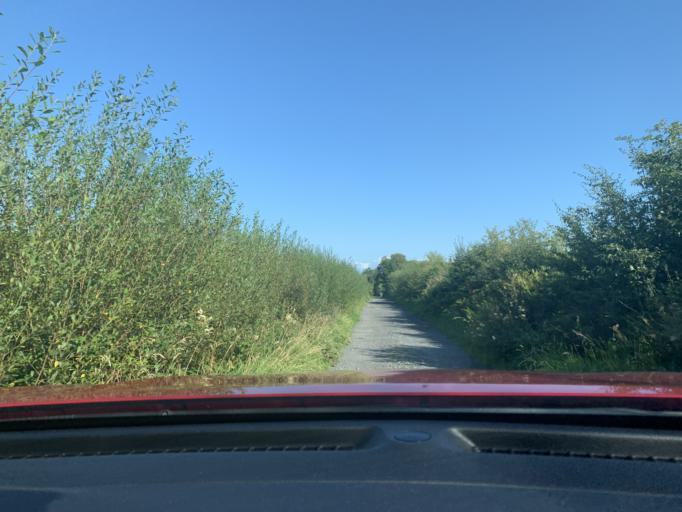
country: IE
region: Connaught
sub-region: Sligo
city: Tobercurry
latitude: 54.0643
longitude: -8.7862
